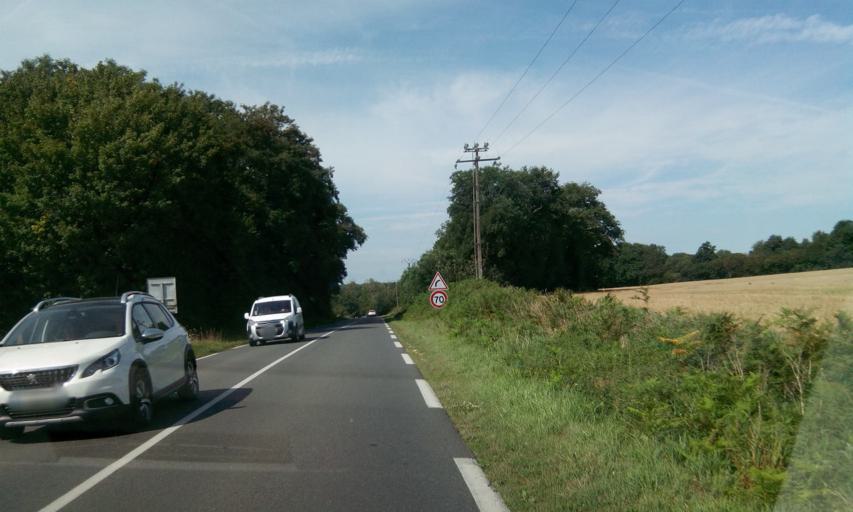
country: FR
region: Poitou-Charentes
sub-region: Departement de la Vienne
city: Savigne
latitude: 46.1581
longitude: 0.3397
